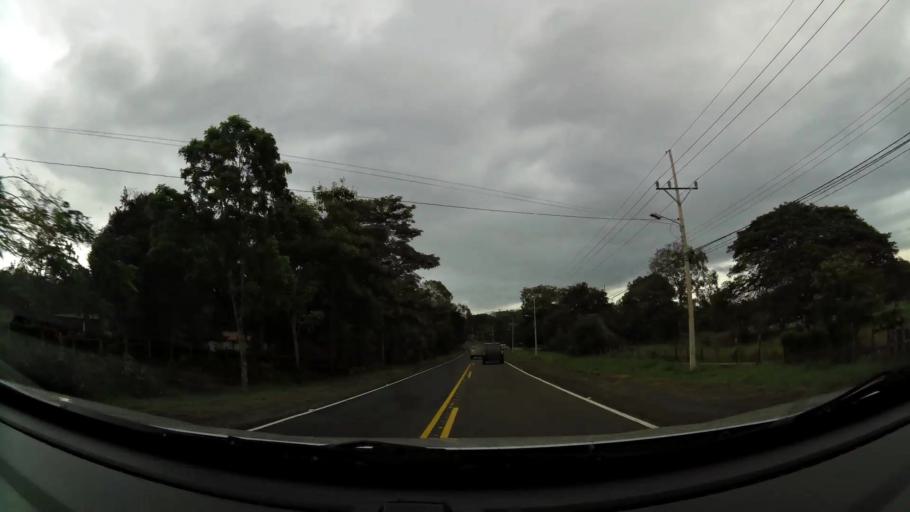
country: CR
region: Alajuela
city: Orotina
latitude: 9.9472
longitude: -84.5640
